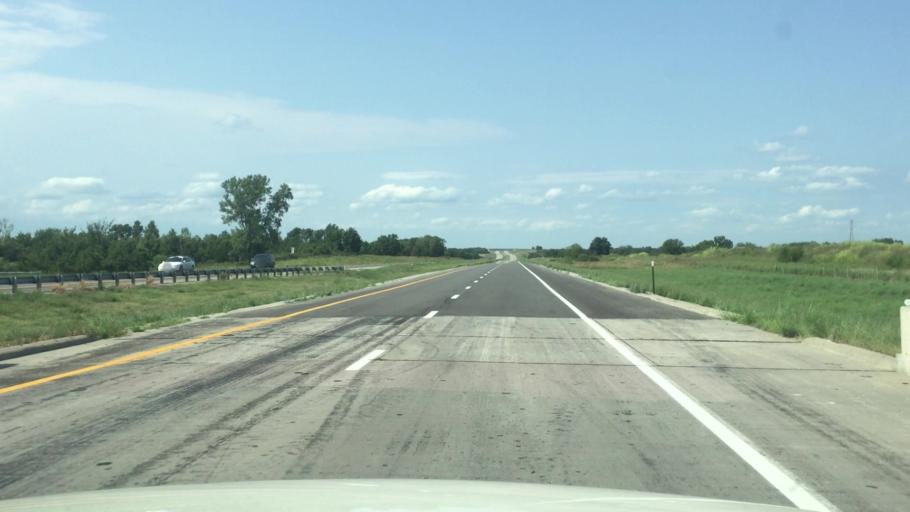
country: US
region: Kansas
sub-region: Linn County
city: La Cygne
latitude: 38.3746
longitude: -94.6874
